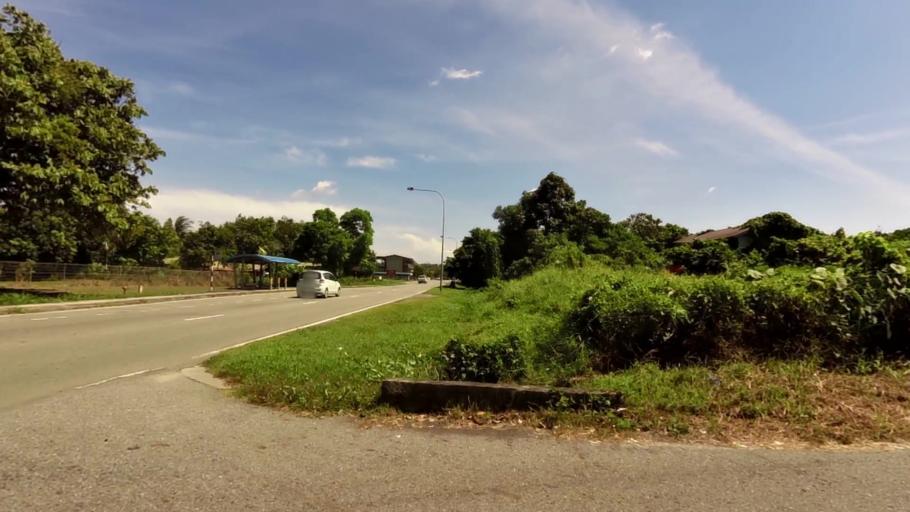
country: BN
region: Brunei and Muara
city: Bandar Seri Begawan
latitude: 4.9378
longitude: 114.9444
